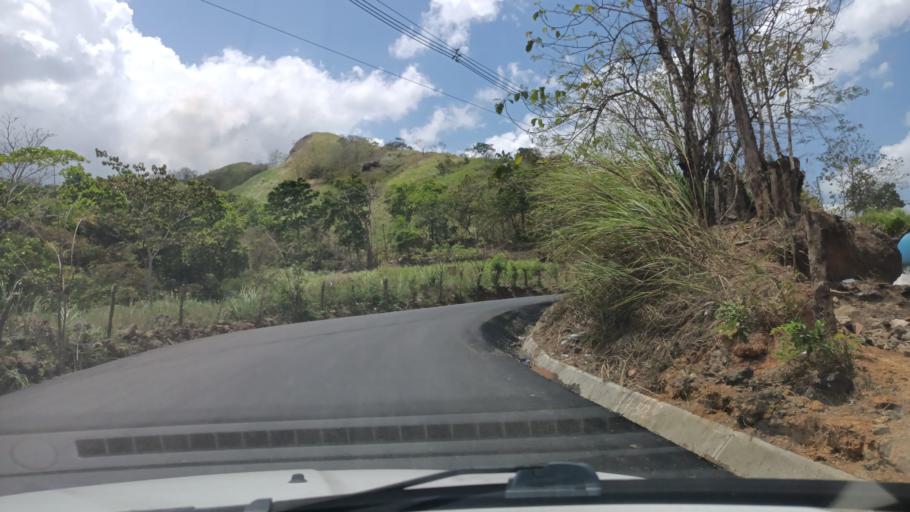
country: PA
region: Panama
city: Alcalde Diaz
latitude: 9.0990
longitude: -79.5676
